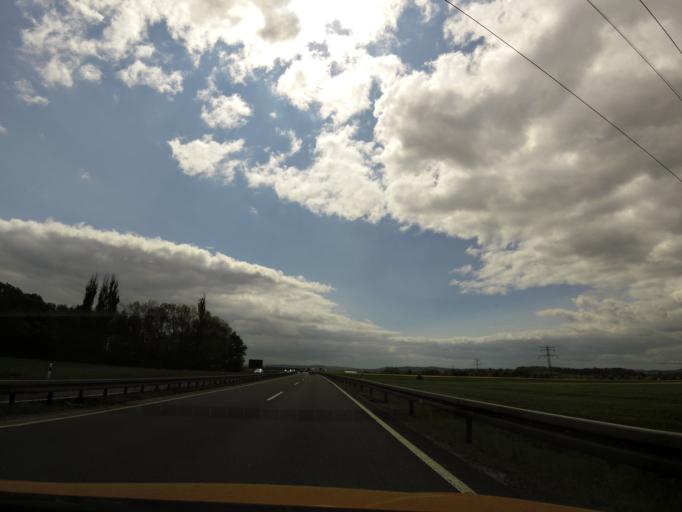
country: DE
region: Lower Saxony
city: Lengede
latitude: 52.1644
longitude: 10.3648
